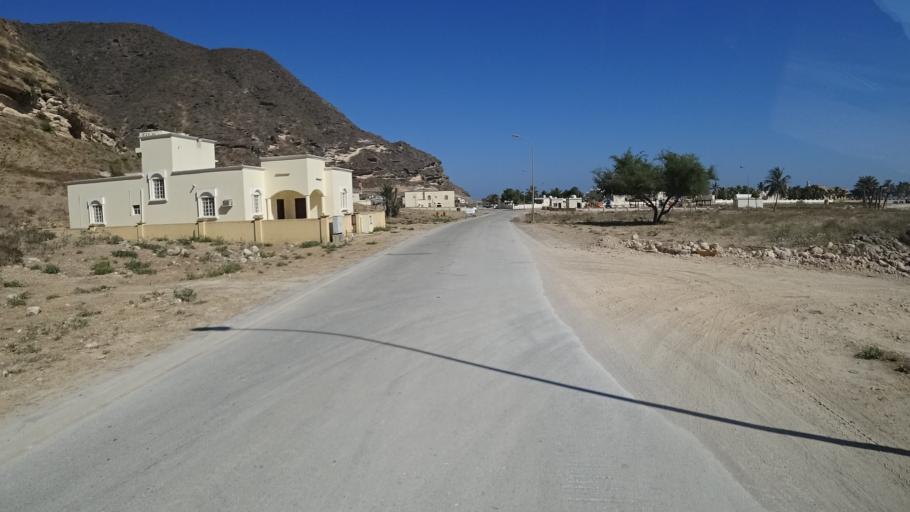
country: YE
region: Al Mahrah
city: Hawf
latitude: 16.7497
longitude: 53.4203
